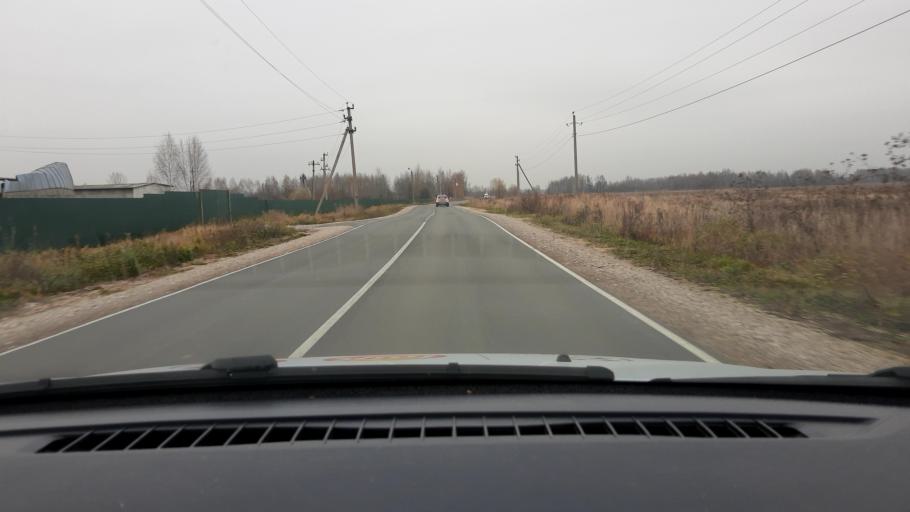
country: RU
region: Nizjnij Novgorod
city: Neklyudovo
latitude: 56.4511
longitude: 43.9016
